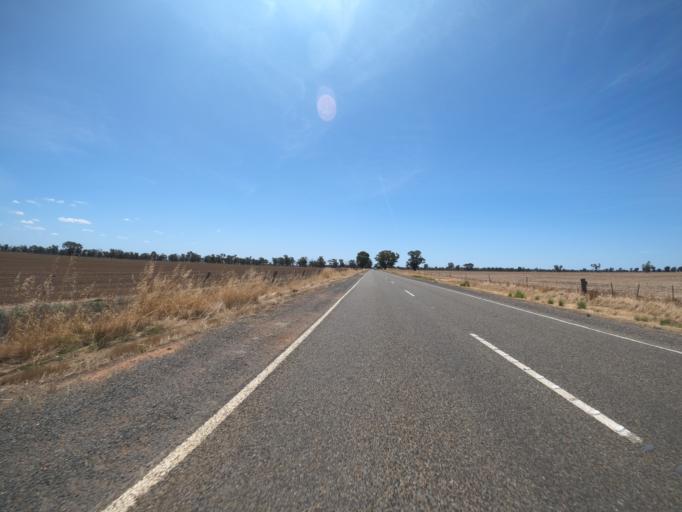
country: AU
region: Victoria
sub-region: Moira
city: Yarrawonga
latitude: -36.1763
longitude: 145.9672
